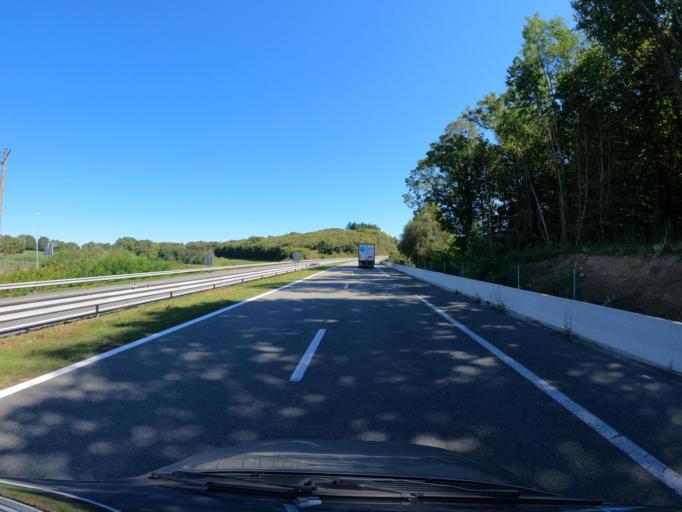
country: FR
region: Limousin
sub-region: Departement de la Creuse
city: Saint-Agnant-de-Versillat
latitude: 46.2375
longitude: 1.5349
